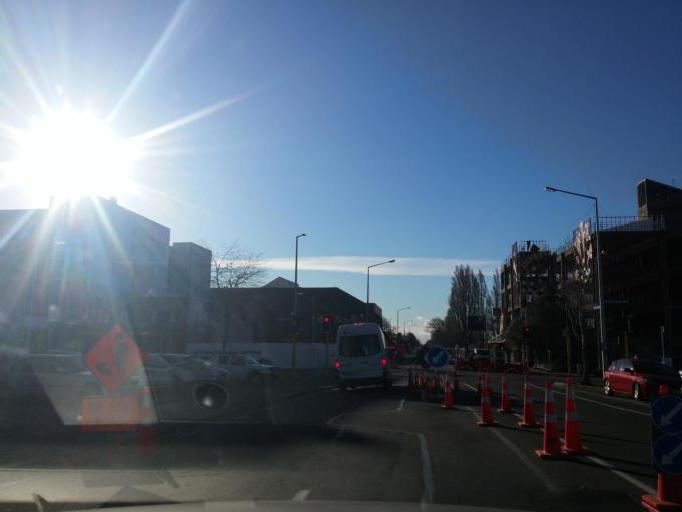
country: NZ
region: Canterbury
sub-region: Christchurch City
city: Christchurch
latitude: -43.5302
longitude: 172.6396
